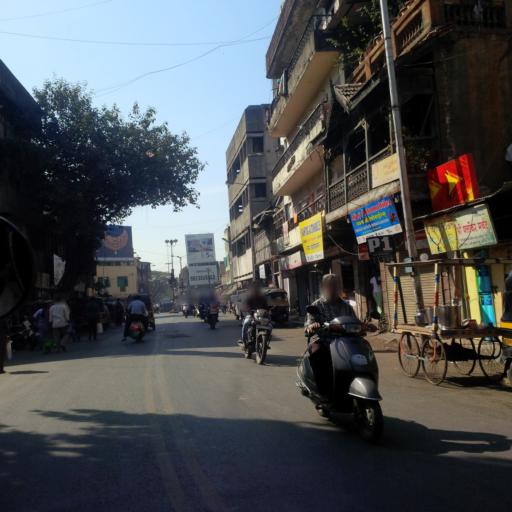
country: IN
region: Maharashtra
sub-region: Pune Division
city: Pune
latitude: 18.5155
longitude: 73.8695
